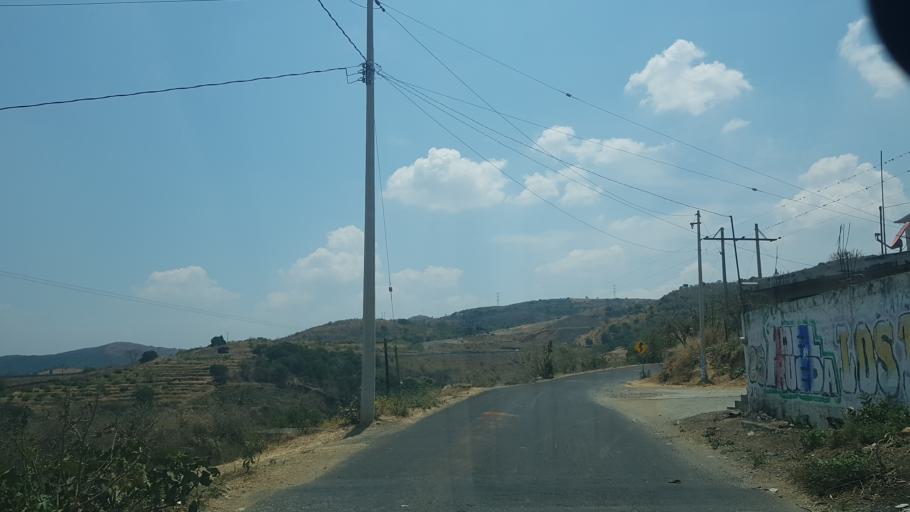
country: MX
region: Puebla
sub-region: Atzitzihuacan
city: Santiago Atzitzihuacan
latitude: 18.8347
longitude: -98.5969
